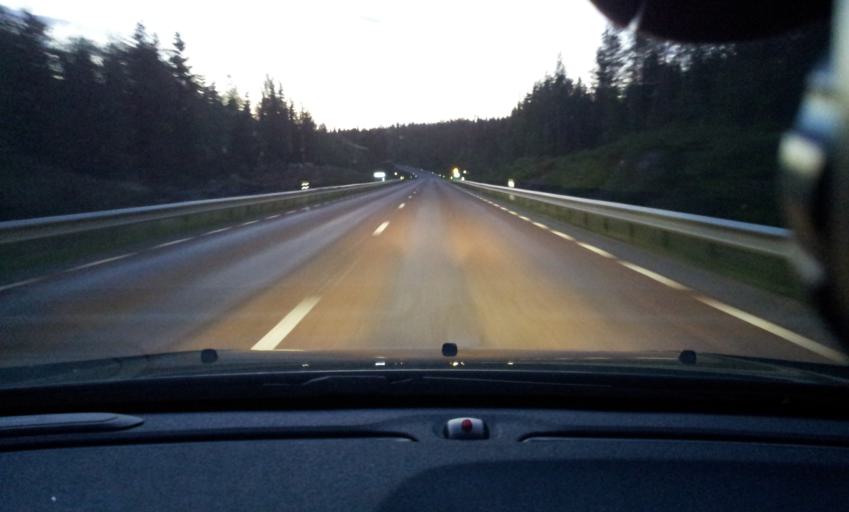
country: SE
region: Jaemtland
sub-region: Bergs Kommun
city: Hoverberg
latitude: 62.8682
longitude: 14.5208
